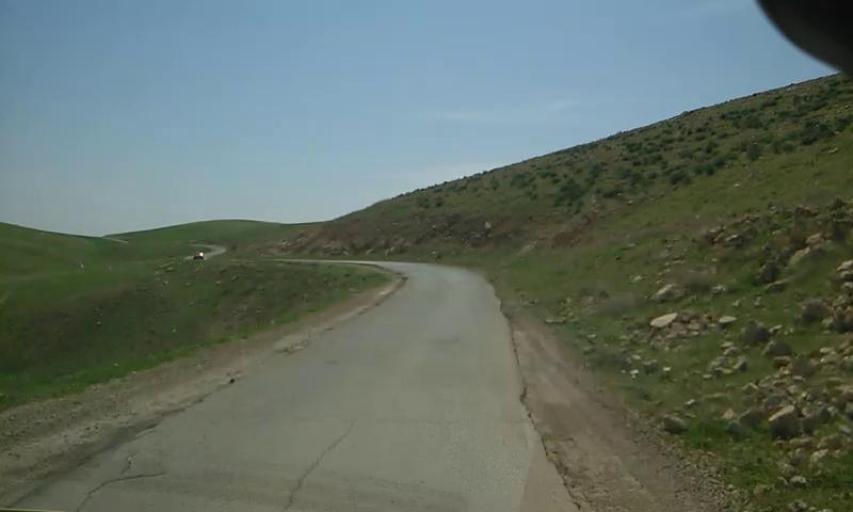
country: PS
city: `Arab ar Rashaydah
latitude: 31.5548
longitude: 35.2493
